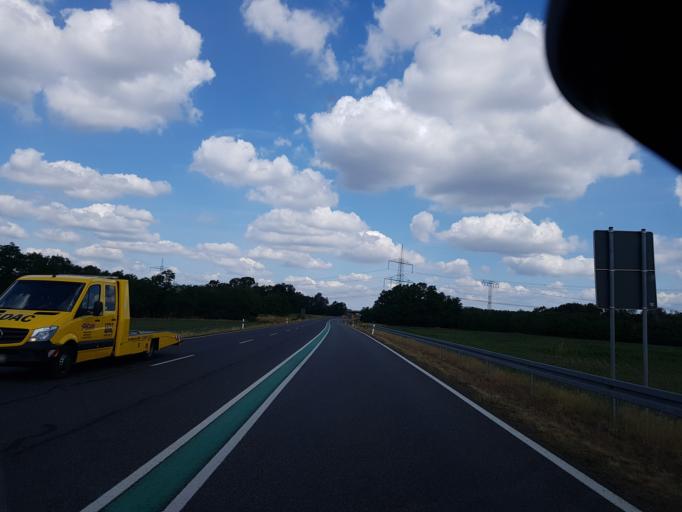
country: DE
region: Brandenburg
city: Drebkau
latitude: 51.6576
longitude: 14.2428
